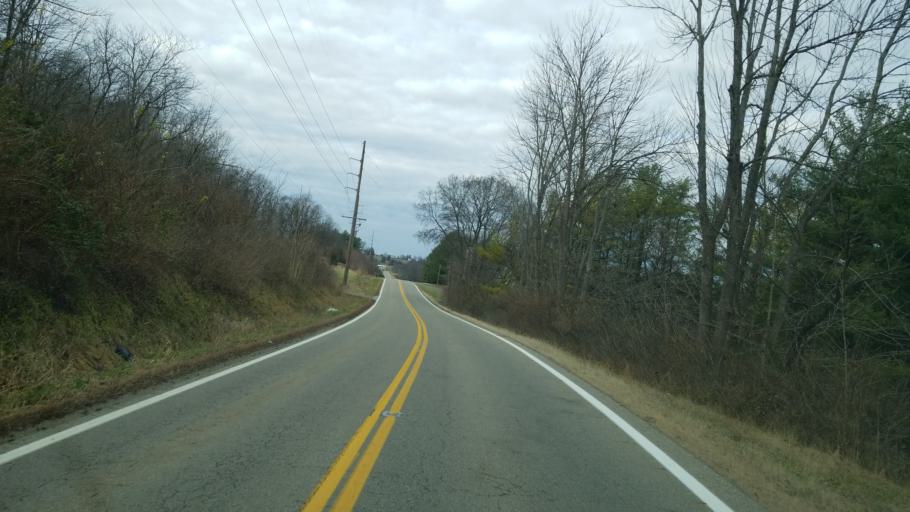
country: US
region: Ohio
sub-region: Ross County
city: Frankfort
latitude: 39.3507
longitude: -83.2240
